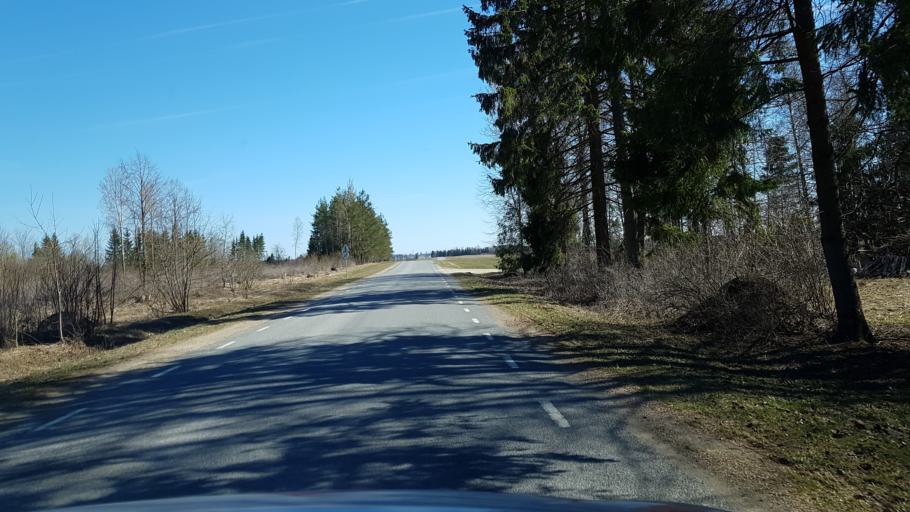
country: EE
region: Laeaene-Virumaa
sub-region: Someru vald
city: Someru
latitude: 59.3606
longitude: 26.4701
